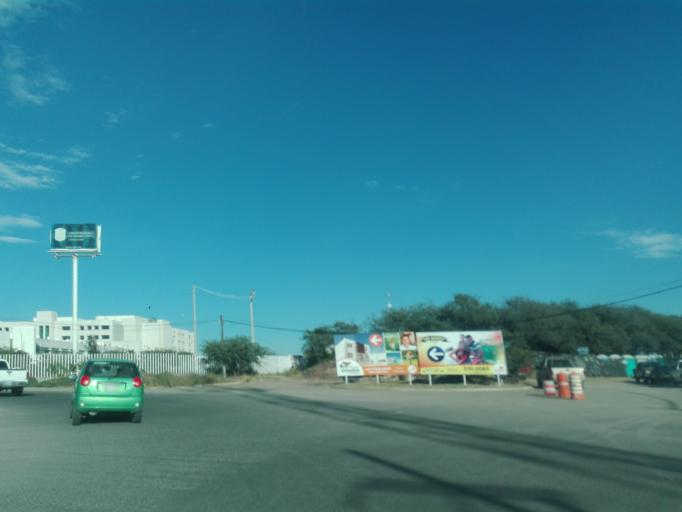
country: MX
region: Guanajuato
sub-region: Leon
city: Ladrilleras del Refugio
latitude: 21.0606
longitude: -101.5747
